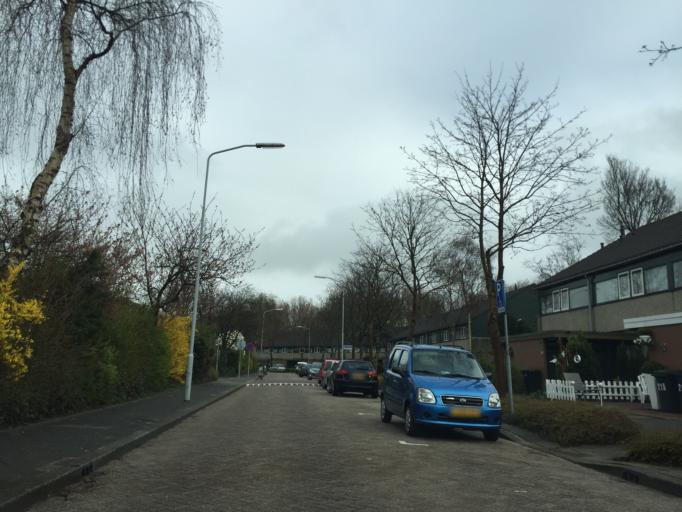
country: NL
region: South Holland
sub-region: Gemeente Leidschendam-Voorburg
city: Voorburg
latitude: 52.0769
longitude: 4.3965
